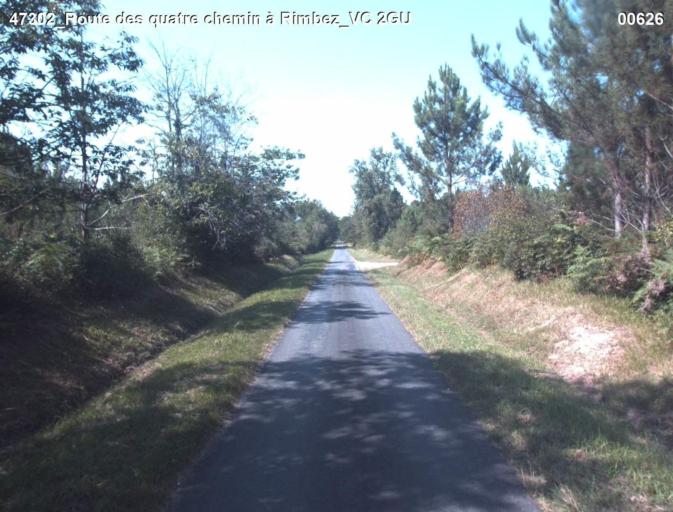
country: FR
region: Aquitaine
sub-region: Departement des Landes
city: Gabarret
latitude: 44.0273
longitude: 0.0833
